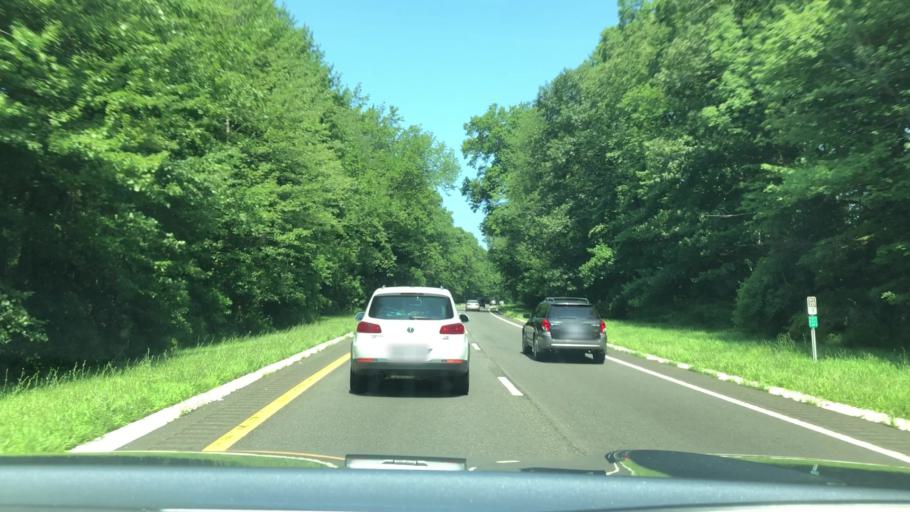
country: US
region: New York
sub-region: Rockland County
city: New Square
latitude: 41.1255
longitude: -74.0125
